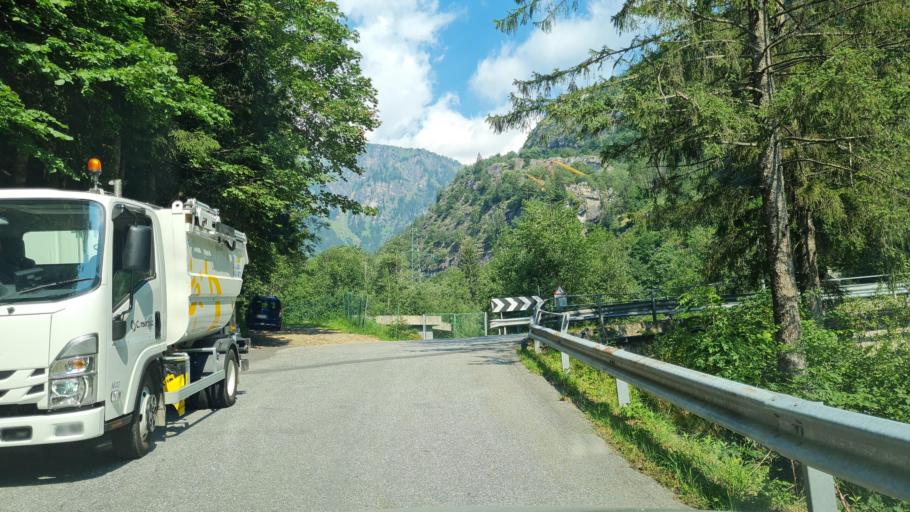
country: IT
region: Piedmont
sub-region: Provincia Verbano-Cusio-Ossola
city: Baceno
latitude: 46.2846
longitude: 8.2870
